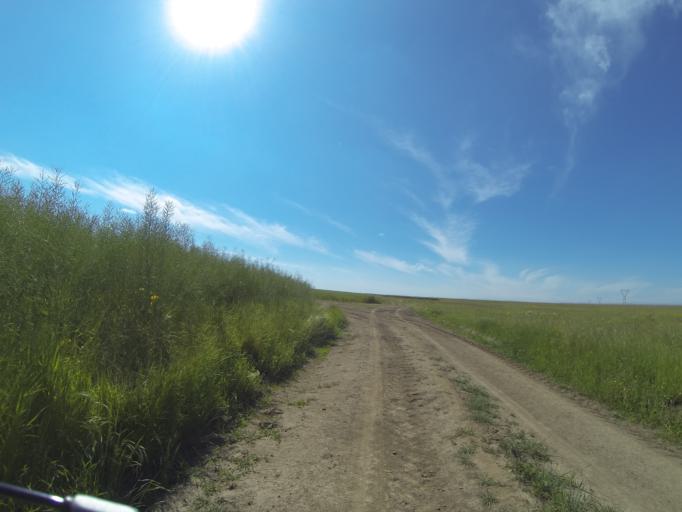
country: RO
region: Dolj
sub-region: Comuna Cosoveni
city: Cosoveni
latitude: 44.2594
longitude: 24.0006
